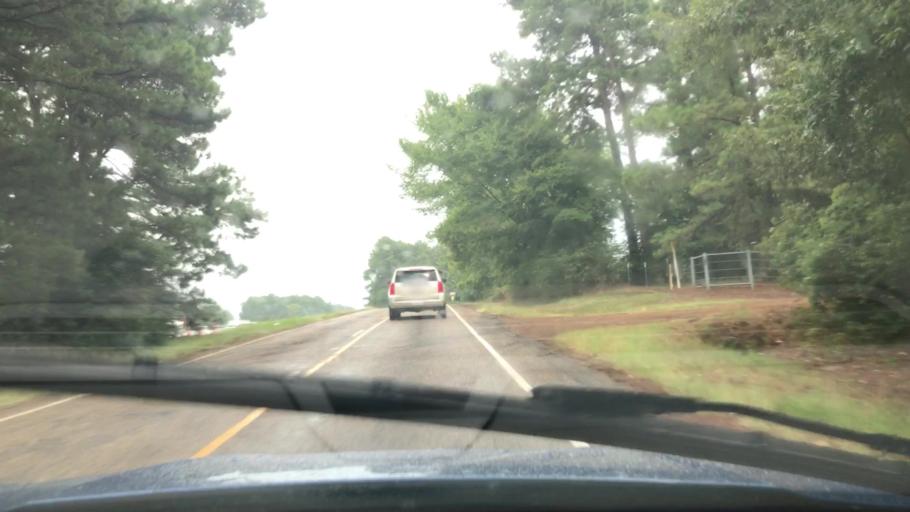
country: US
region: Texas
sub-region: Harrison County
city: Waskom
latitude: 32.4845
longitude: -94.1188
